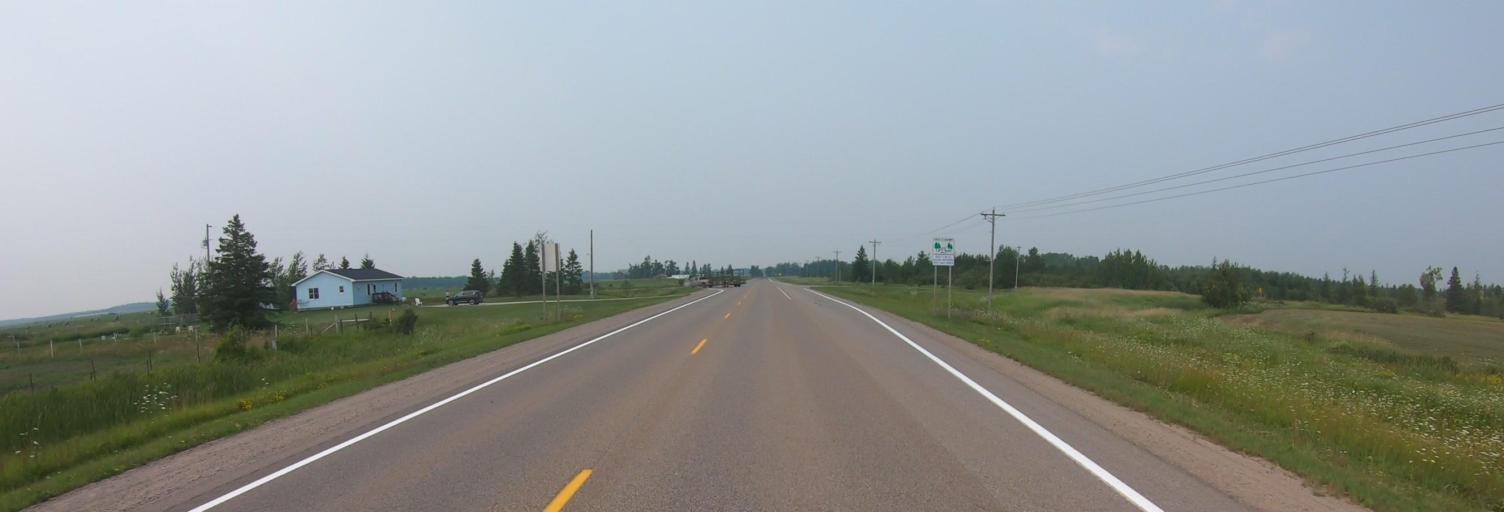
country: US
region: Michigan
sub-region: Chippewa County
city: Sault Ste. Marie
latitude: 46.3600
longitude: -84.3640
